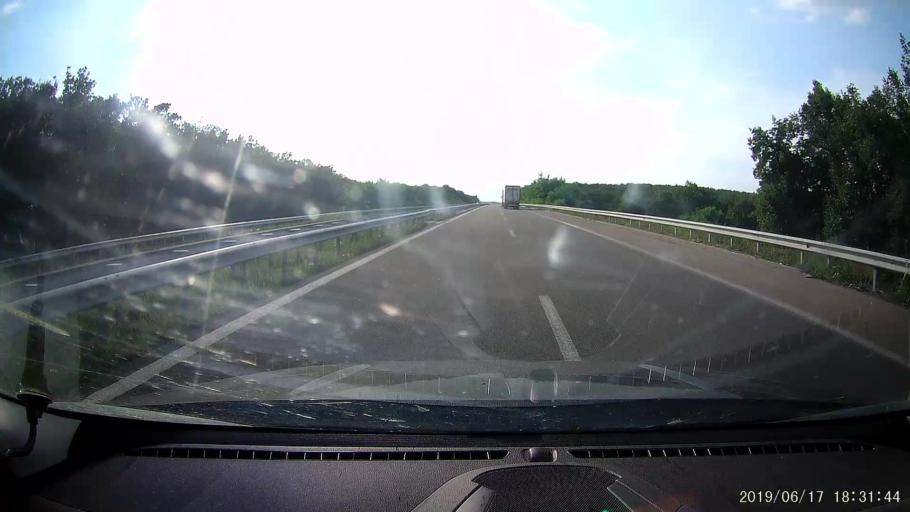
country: BG
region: Khaskovo
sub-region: Obshtina Dimitrovgrad
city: Dimitrovgrad
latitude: 42.0502
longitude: 25.4966
